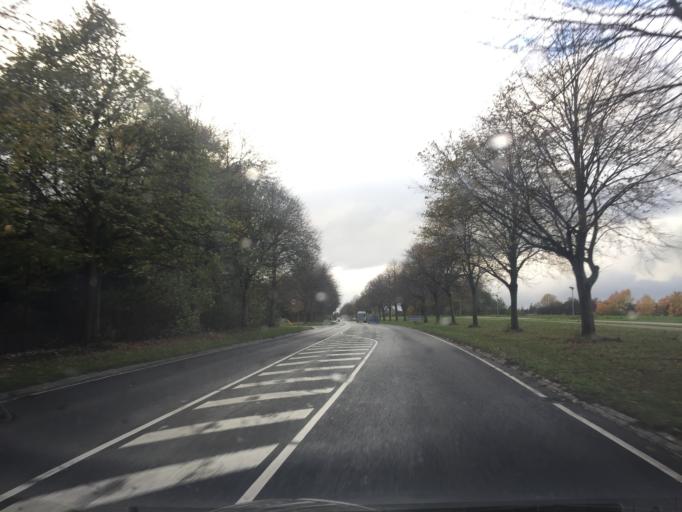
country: DK
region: Capital Region
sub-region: Fredensborg Kommune
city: Humlebaek
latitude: 55.9671
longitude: 12.5080
